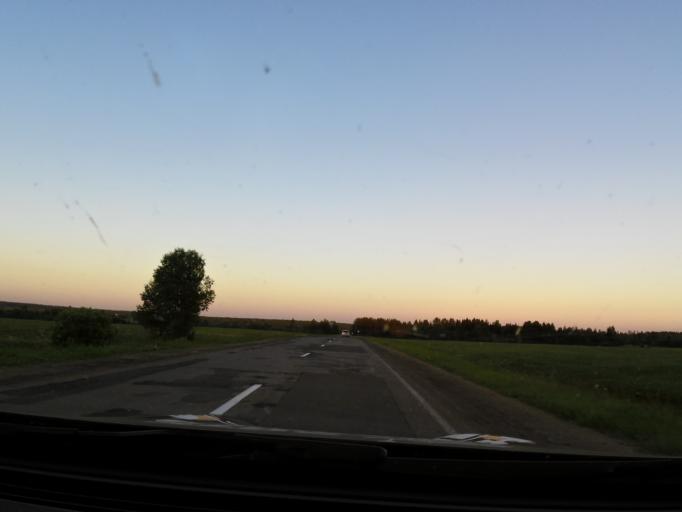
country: RU
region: Jaroslavl
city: Lyubim
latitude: 58.3545
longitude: 40.7794
